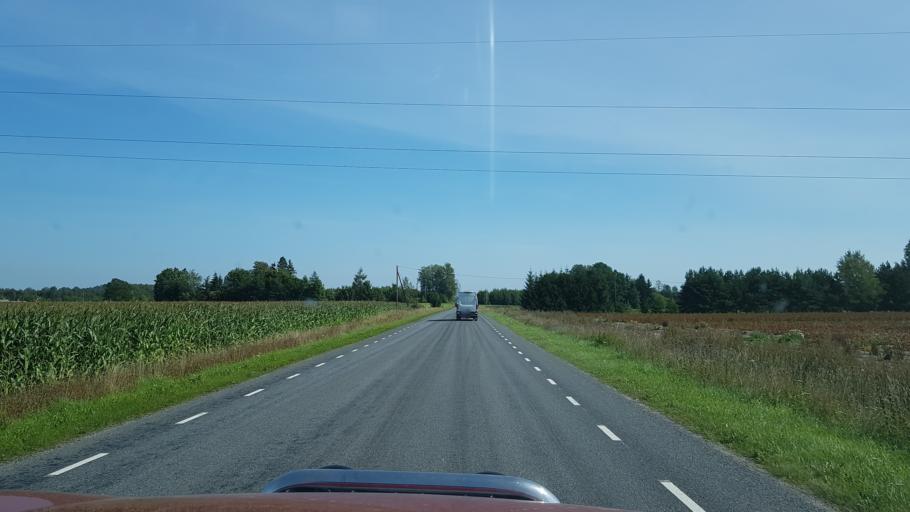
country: EE
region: Viljandimaa
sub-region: Suure-Jaani vald
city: Suure-Jaani
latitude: 58.4880
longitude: 25.5279
